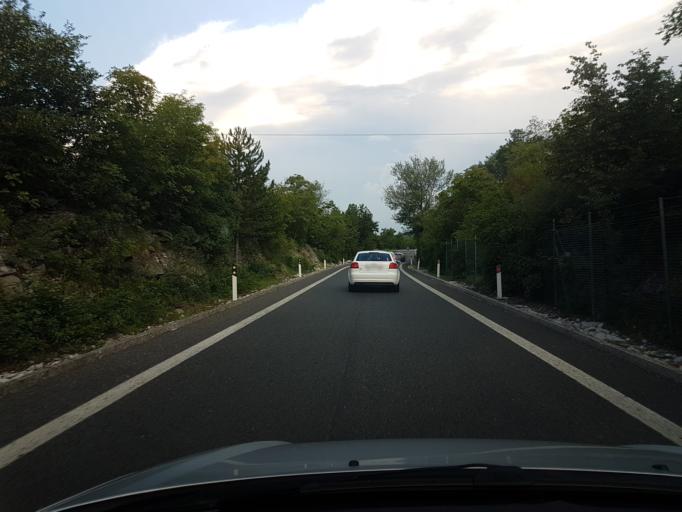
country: IT
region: Friuli Venezia Giulia
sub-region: Provincia di Trieste
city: Sistiana-Visogliano
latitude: 45.7705
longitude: 13.6459
